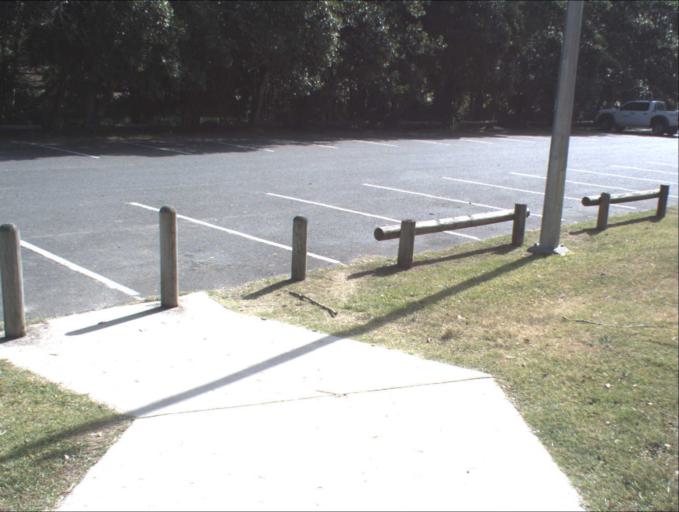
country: AU
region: Queensland
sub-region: Logan
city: Springwood
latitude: -27.6019
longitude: 153.1475
